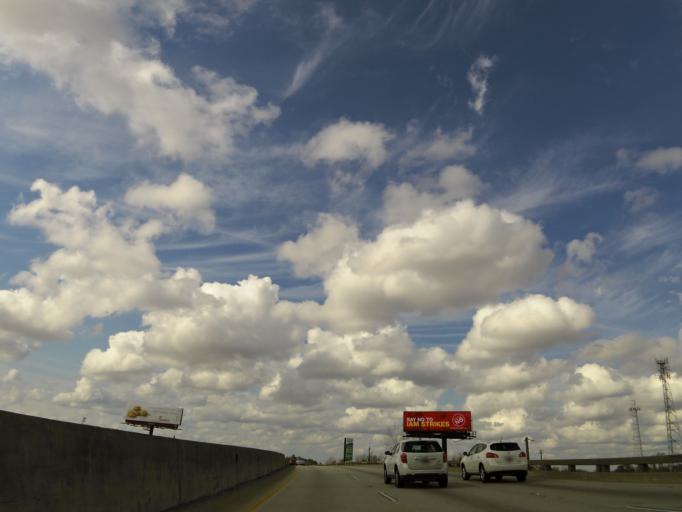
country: US
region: South Carolina
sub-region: Charleston County
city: North Charleston
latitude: 32.8645
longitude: -79.9976
